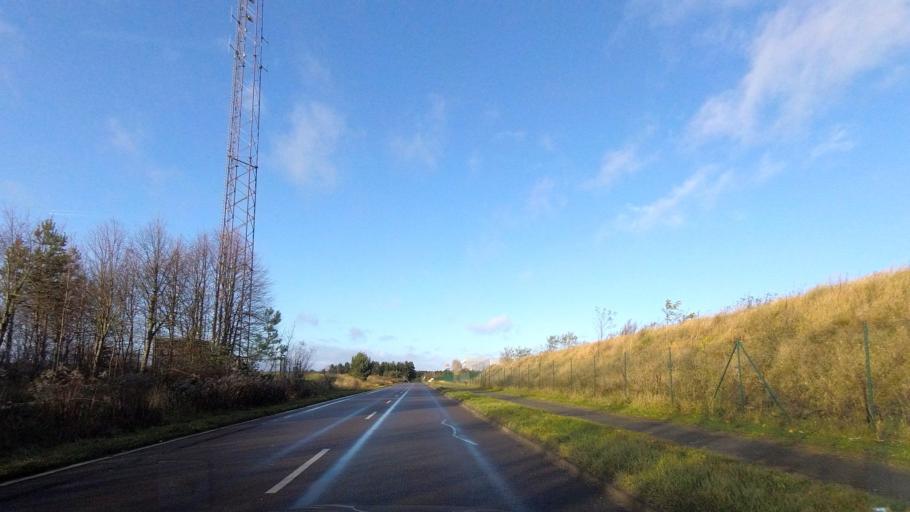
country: DE
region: Brandenburg
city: Niemegk
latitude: 52.0861
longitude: 12.7048
